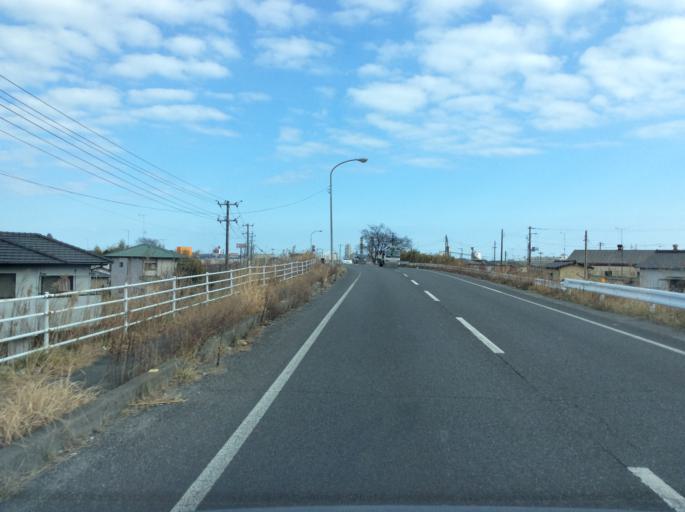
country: JP
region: Fukushima
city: Iwaki
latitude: 36.9507
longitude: 140.8794
